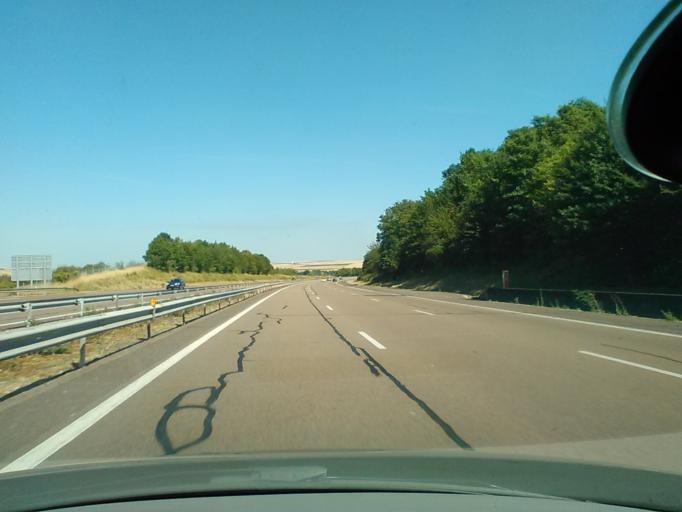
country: FR
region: Bourgogne
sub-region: Departement de l'Yonne
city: Aillant-sur-Tholon
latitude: 47.9113
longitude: 3.3220
